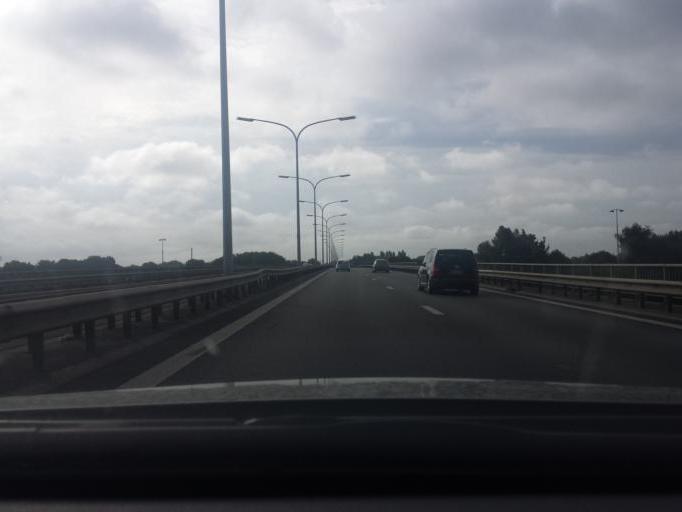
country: BE
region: Flanders
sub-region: Provincie West-Vlaanderen
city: Kortrijk
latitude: 50.8143
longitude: 3.2360
